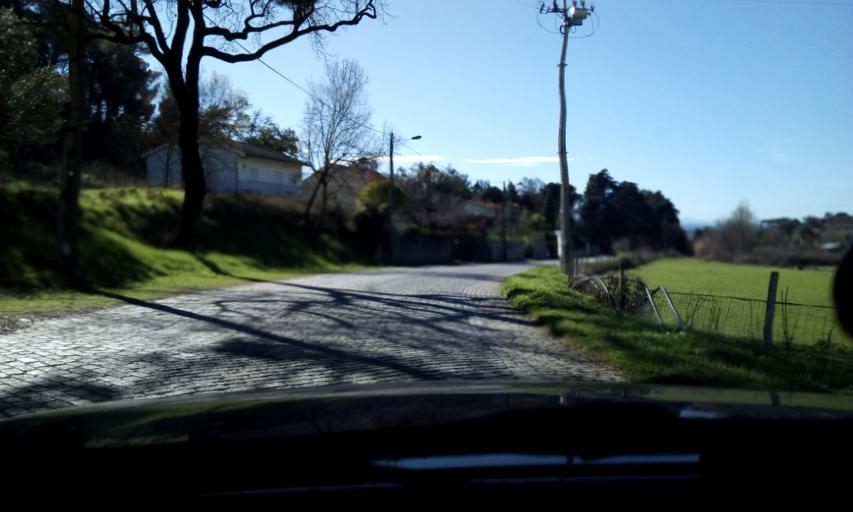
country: PT
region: Guarda
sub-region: Fornos de Algodres
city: Fornos de Algodres
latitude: 40.6204
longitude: -7.5302
